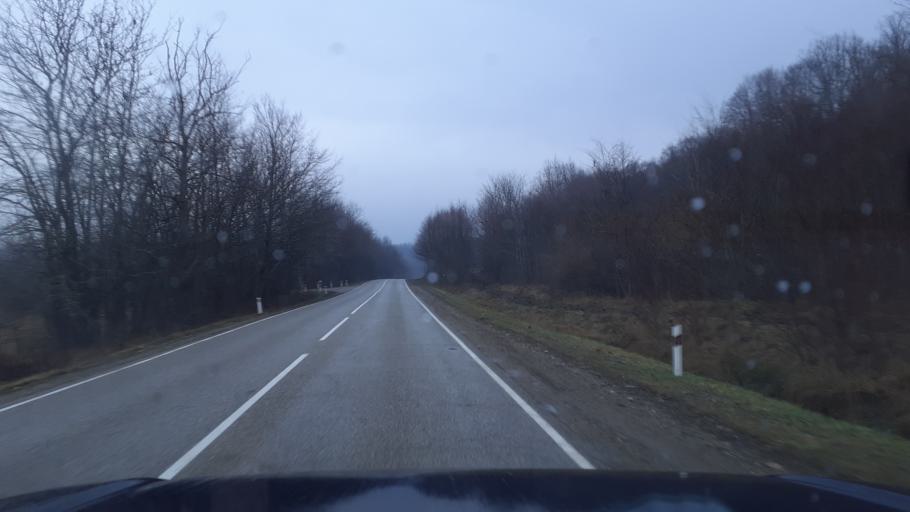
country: RU
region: Krasnodarskiy
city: Neftegorsk
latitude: 44.3144
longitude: 39.8327
